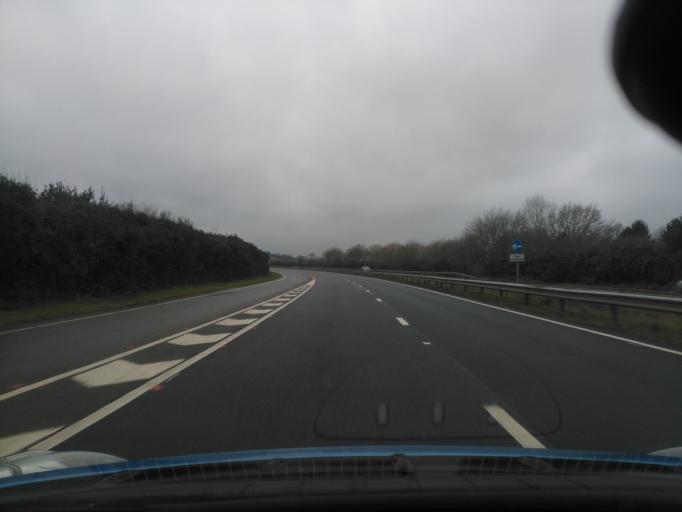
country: GB
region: England
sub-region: Surrey
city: Elstead
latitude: 51.1485
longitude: -0.7013
